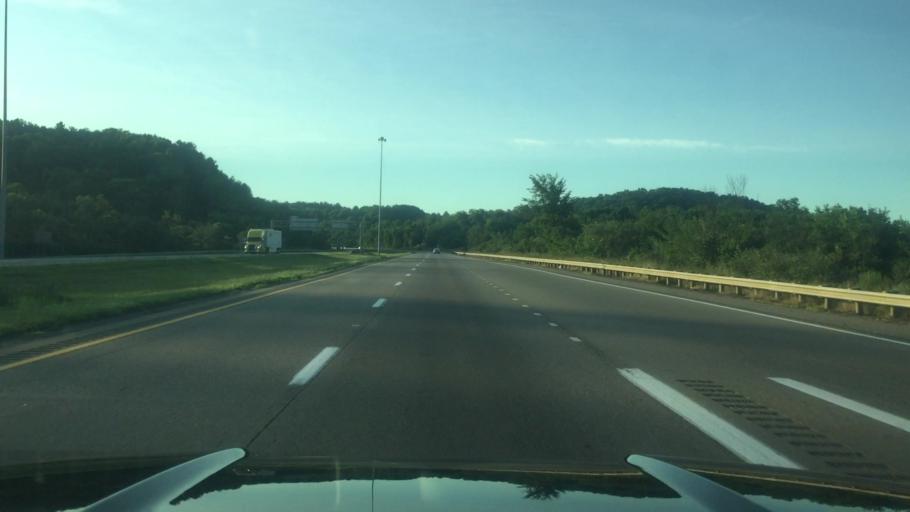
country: US
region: Ohio
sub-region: Tuscarawas County
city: Newcomerstown
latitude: 40.2922
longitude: -81.5571
